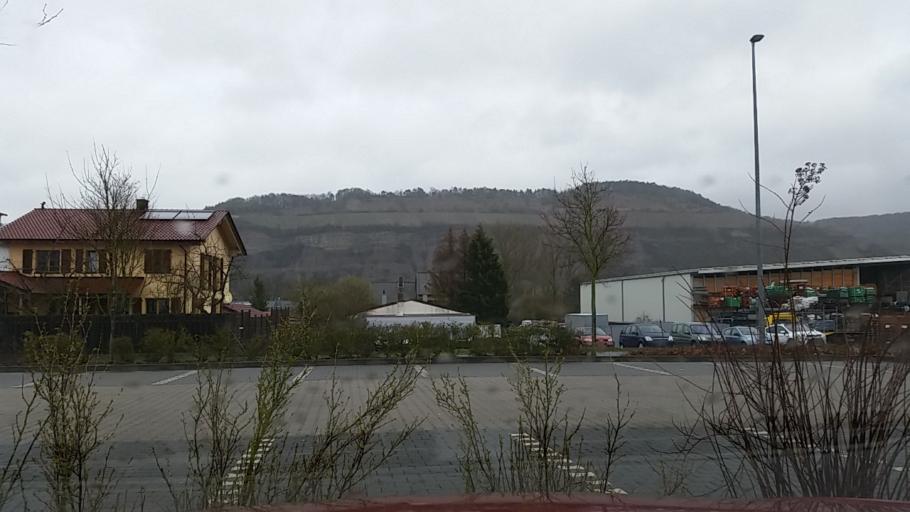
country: DE
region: Bavaria
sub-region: Regierungsbezirk Unterfranken
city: Zellingen
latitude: 49.8921
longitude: 9.8243
